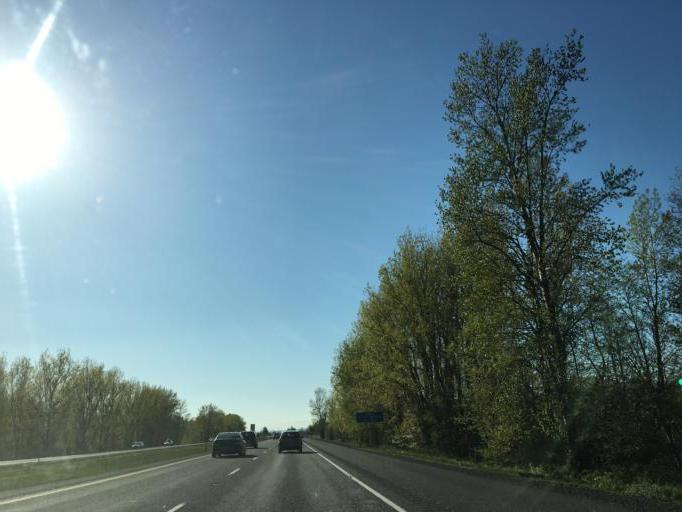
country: US
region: Oregon
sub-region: Multnomah County
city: Troutdale
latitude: 45.5438
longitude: -122.3694
